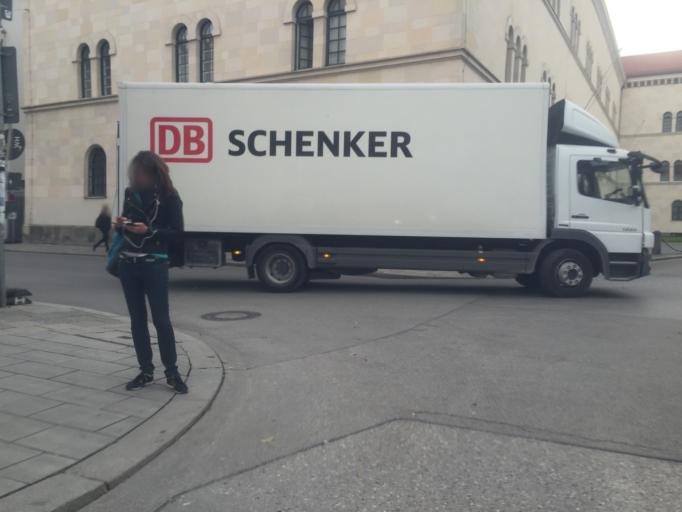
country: DE
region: Bavaria
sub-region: Upper Bavaria
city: Munich
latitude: 48.1506
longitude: 11.5821
